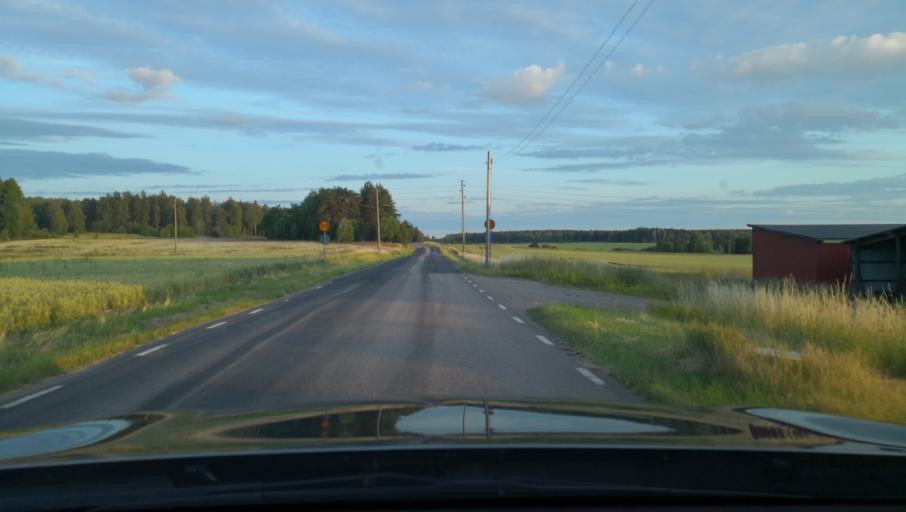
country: SE
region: Uppsala
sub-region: Uppsala Kommun
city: Vattholma
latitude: 60.0197
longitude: 17.7211
